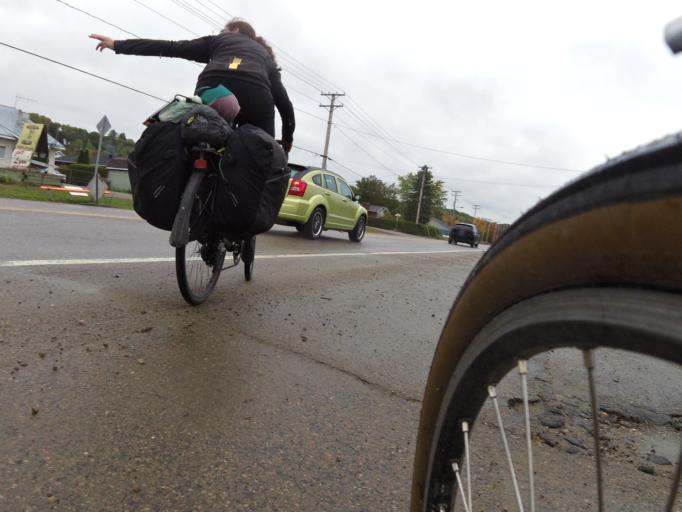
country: CA
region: Quebec
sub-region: Outaouais
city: Fort-Coulonge
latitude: 45.8486
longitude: -76.7247
